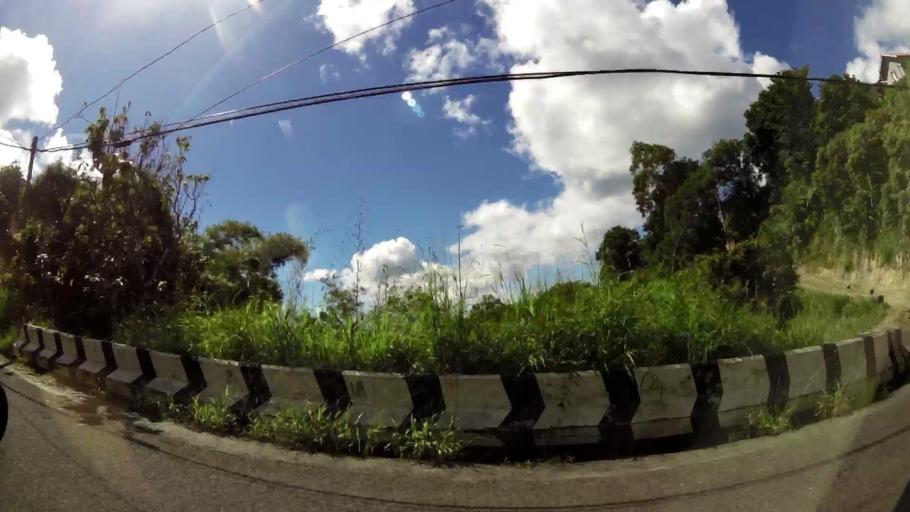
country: TT
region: Tobago
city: Scarborough
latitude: 11.2401
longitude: -60.7338
